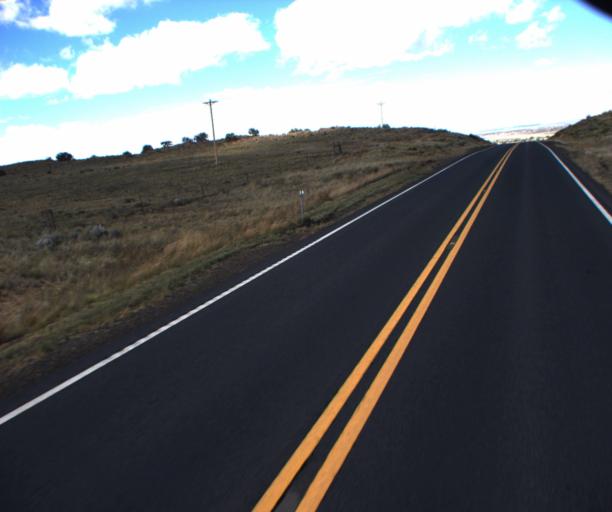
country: US
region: Arizona
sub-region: Apache County
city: Houck
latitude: 35.0331
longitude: -109.2587
